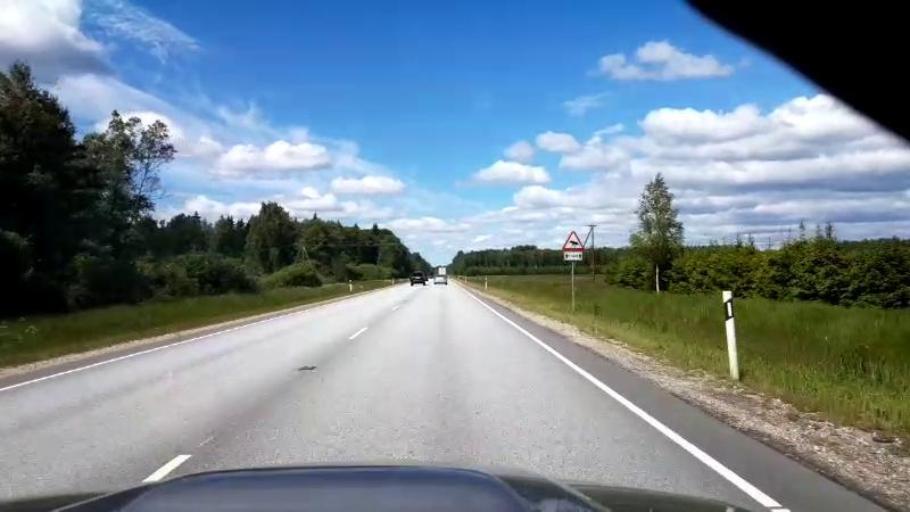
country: EE
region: Paernumaa
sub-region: Halinga vald
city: Parnu-Jaagupi
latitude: 58.5394
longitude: 24.5455
